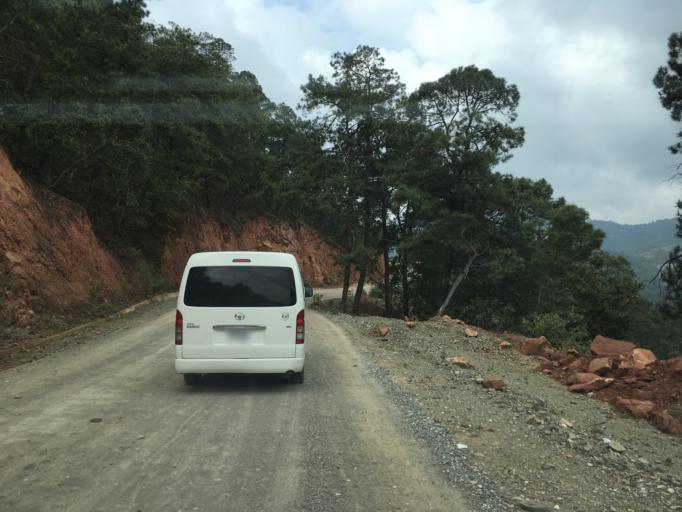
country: MX
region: Oaxaca
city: Santiago Tilantongo
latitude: 17.2050
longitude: -97.2791
